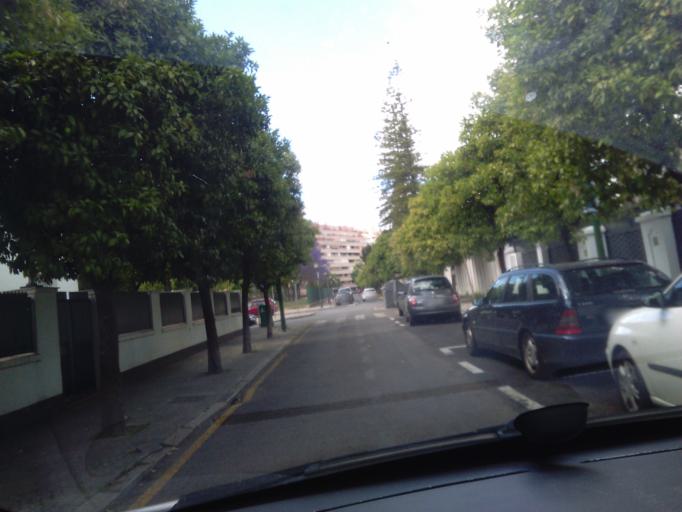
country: ES
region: Andalusia
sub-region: Provincia de Sevilla
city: Sevilla
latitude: 37.3606
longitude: -5.9844
